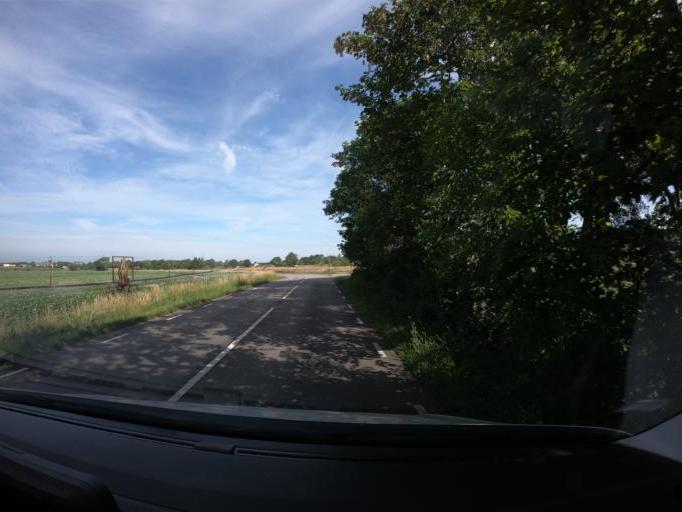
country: SE
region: Skane
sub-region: Angelholms Kommun
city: Vejbystrand
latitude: 56.4129
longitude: 12.6600
